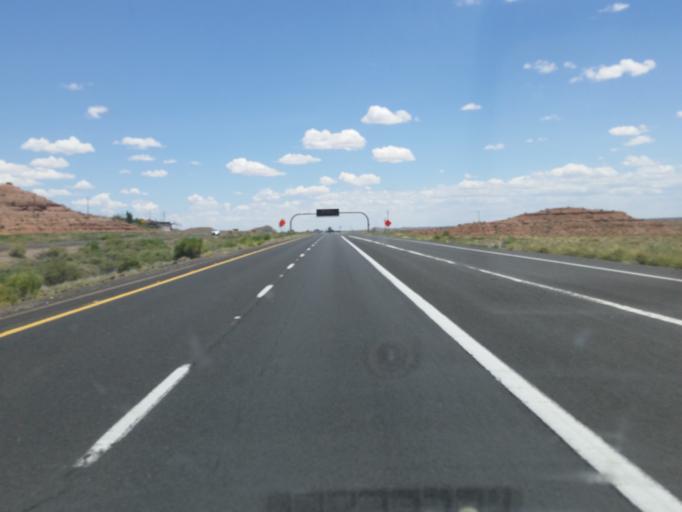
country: US
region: Arizona
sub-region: Navajo County
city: Joseph City
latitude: 34.9211
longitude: -110.2583
